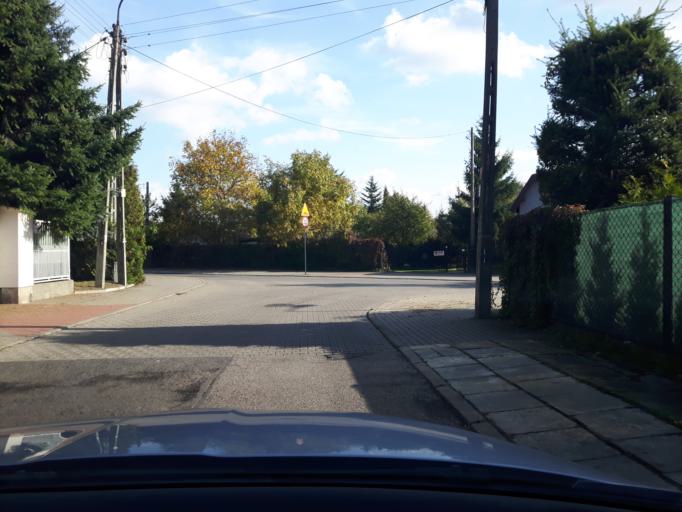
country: PL
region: Masovian Voivodeship
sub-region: Warszawa
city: Targowek
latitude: 52.2783
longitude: 21.0758
